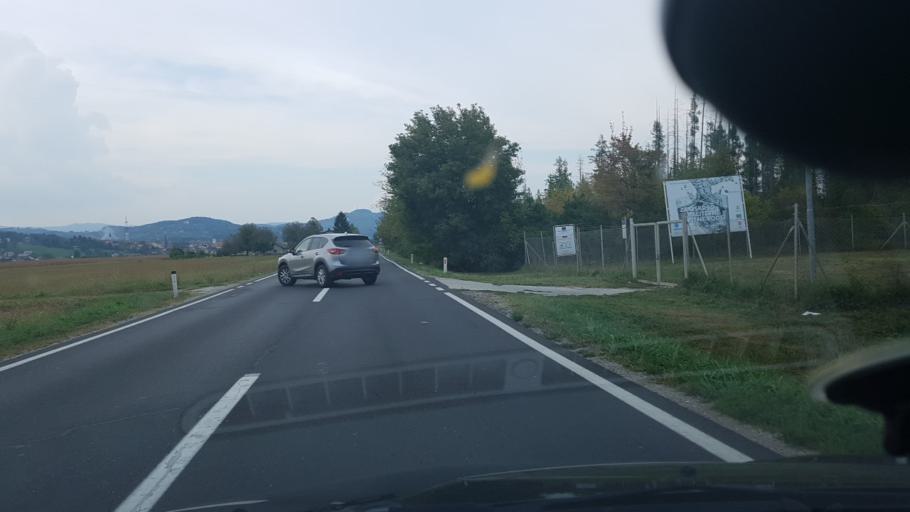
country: SI
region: Krsko
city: Leskovec pri Krskem
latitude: 45.9241
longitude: 15.4772
